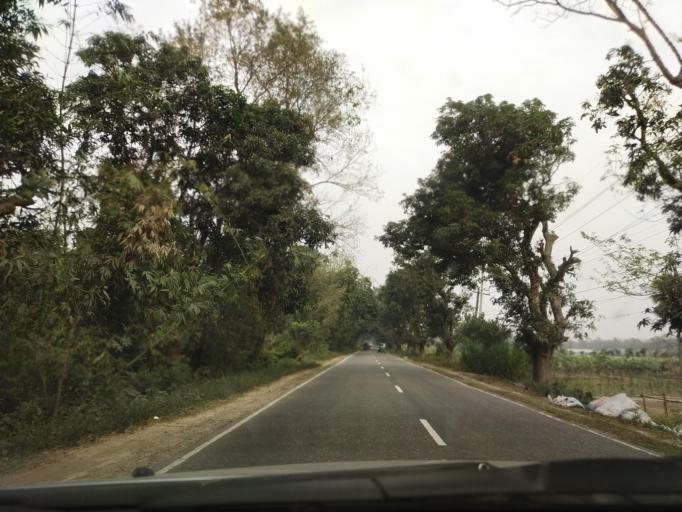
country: BD
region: Dhaka
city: Narsingdi
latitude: 24.0037
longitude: 90.7375
